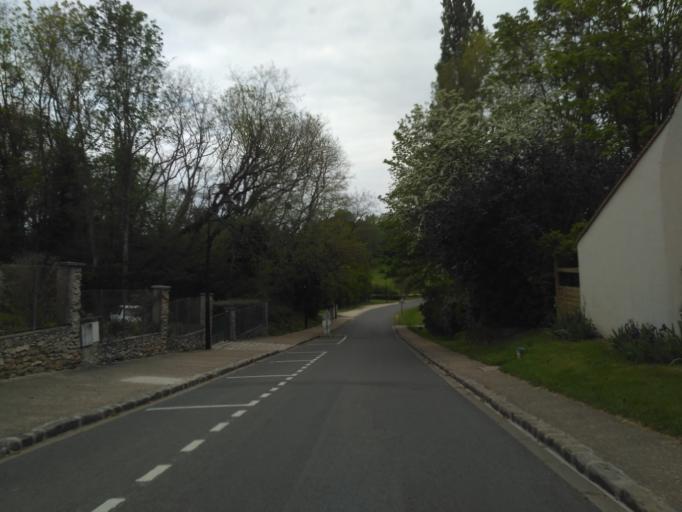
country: FR
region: Ile-de-France
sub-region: Departement de Seine-et-Marne
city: Moisenay
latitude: 48.5695
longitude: 2.7816
